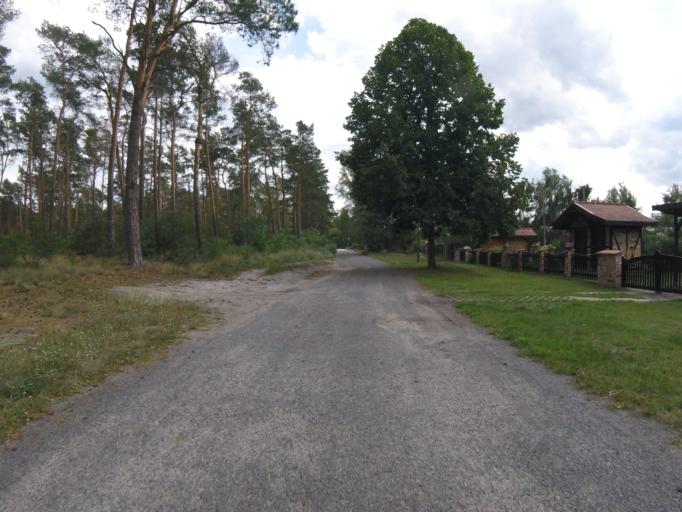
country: DE
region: Brandenburg
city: Halbe
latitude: 52.1167
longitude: 13.7001
